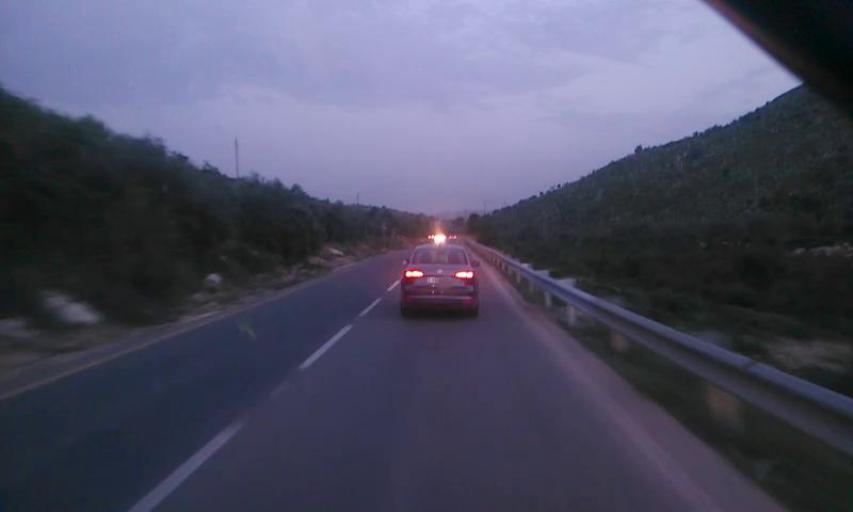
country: PS
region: West Bank
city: Ramin
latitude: 32.2821
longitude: 35.1430
